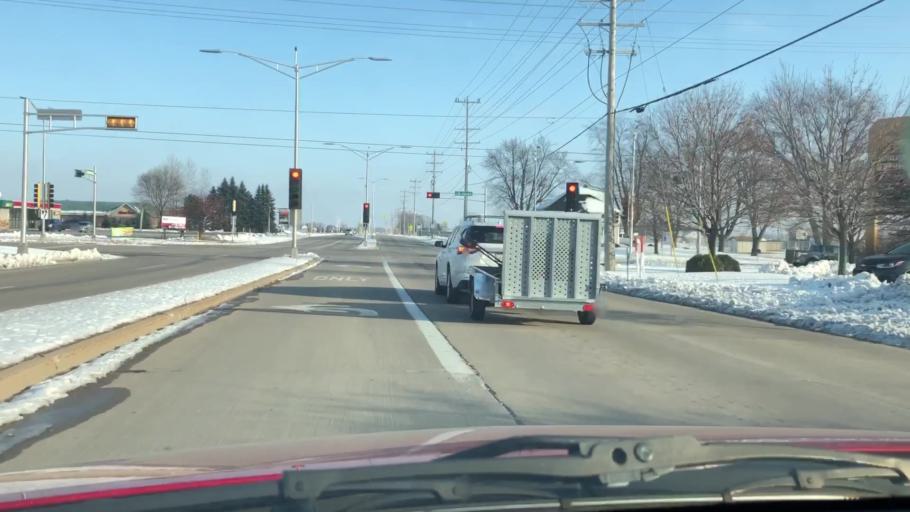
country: US
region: Wisconsin
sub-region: Outagamie County
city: Kimberly
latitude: 44.3165
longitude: -88.3758
